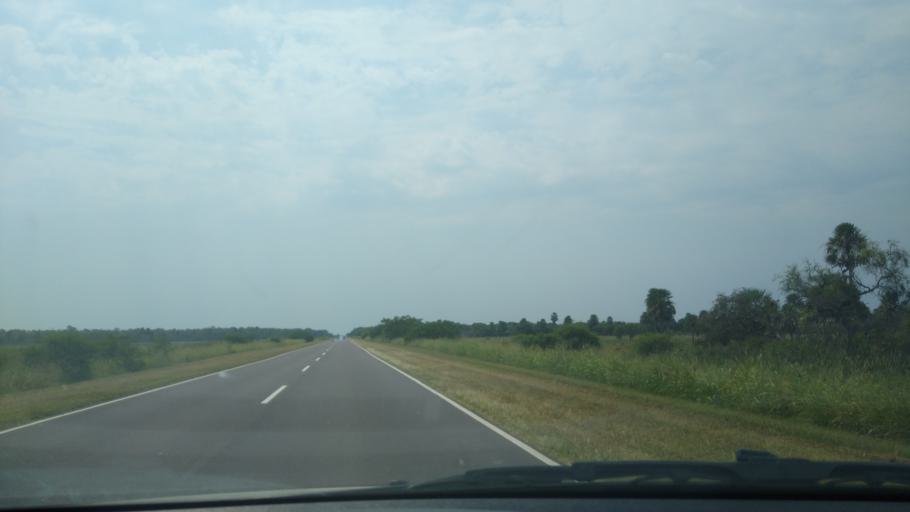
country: AR
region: Chaco
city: La Eduvigis
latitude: -27.0232
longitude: -58.9676
